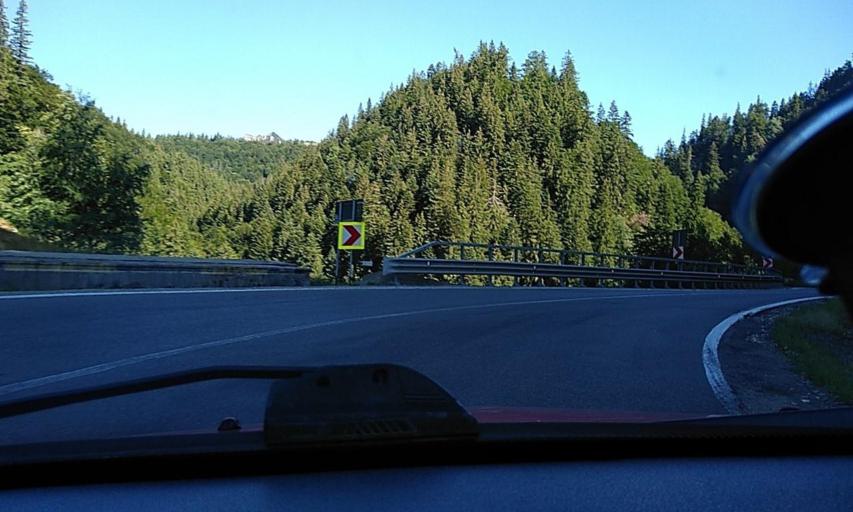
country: RO
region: Brasov
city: Crivina
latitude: 45.4716
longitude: 25.9208
